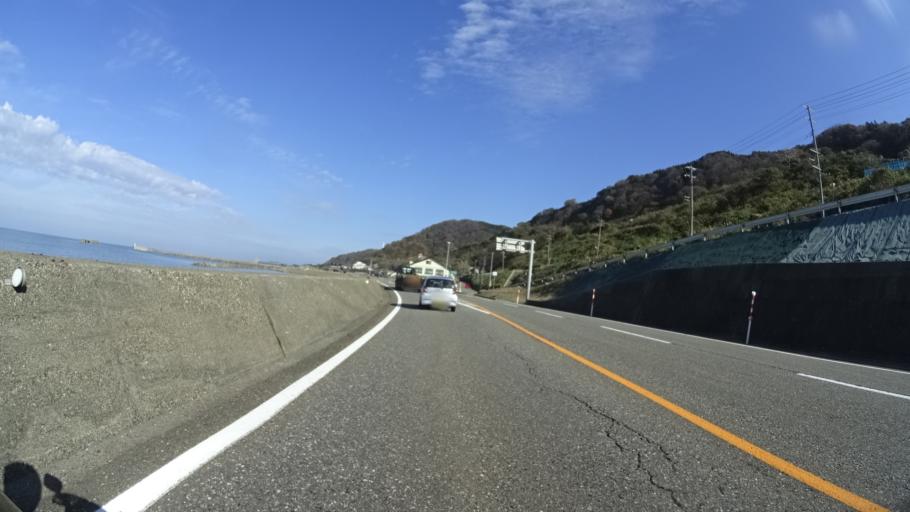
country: JP
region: Niigata
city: Joetsu
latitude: 37.1273
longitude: 138.0481
